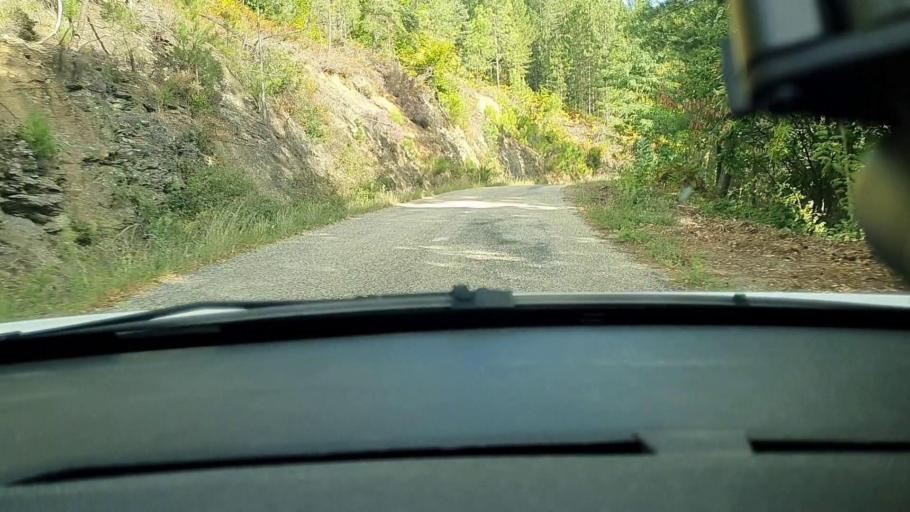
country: FR
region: Languedoc-Roussillon
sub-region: Departement du Gard
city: Besseges
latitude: 44.3499
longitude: 3.9818
